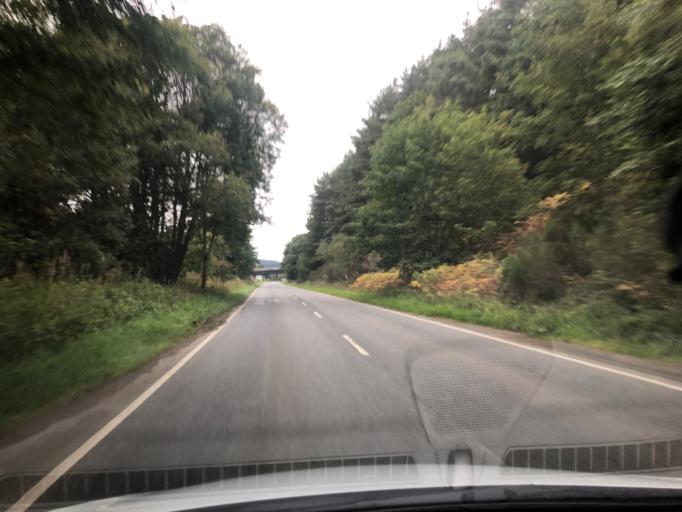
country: GB
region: Scotland
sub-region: Perth and Kinross
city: Pitlochry
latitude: 56.7544
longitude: -3.8084
